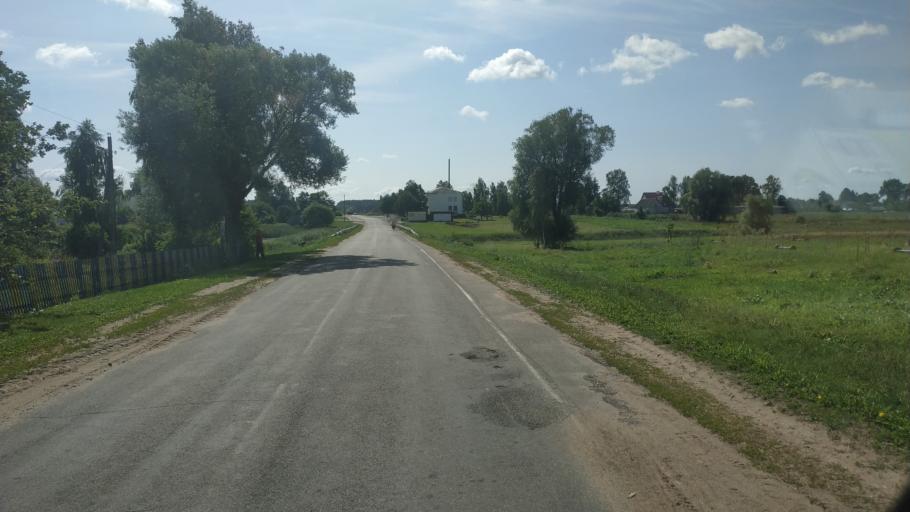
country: BY
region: Mogilev
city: Ramanavichy
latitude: 53.7056
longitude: 30.5038
